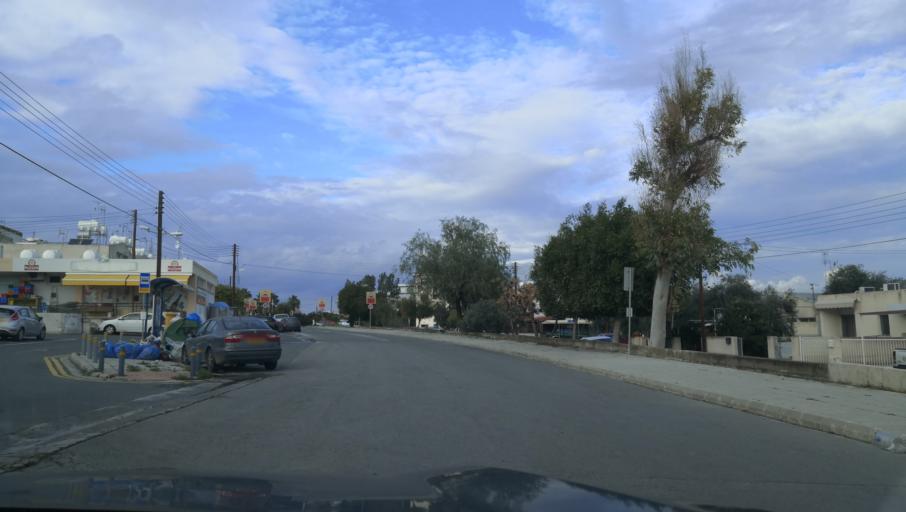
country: CY
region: Lefkosia
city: Nicosia
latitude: 35.1271
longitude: 33.3497
